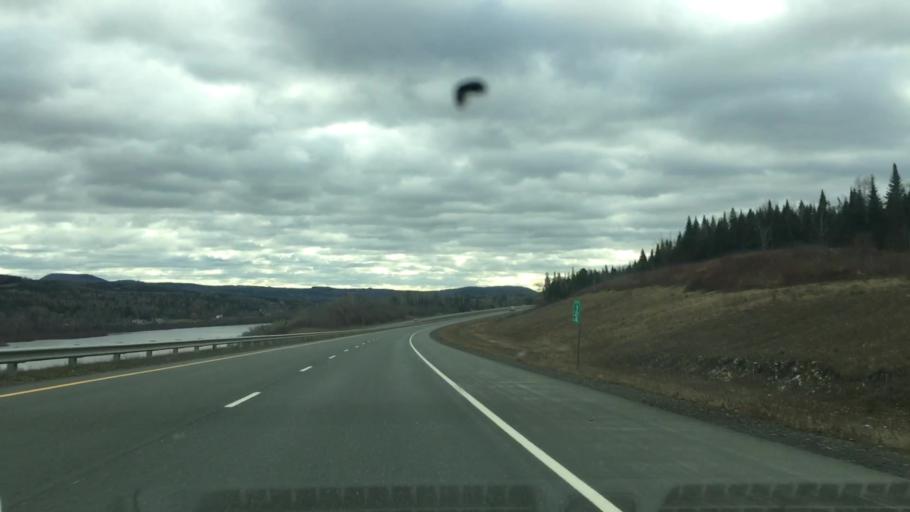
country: US
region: Maine
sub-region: Aroostook County
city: Fort Fairfield
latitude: 46.6805
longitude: -67.7319
